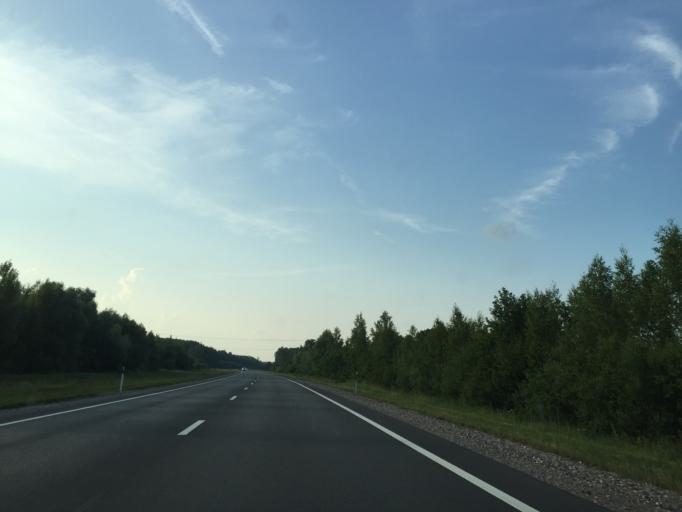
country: LV
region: Ozolnieku
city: Ozolnieki
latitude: 56.6748
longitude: 23.8237
